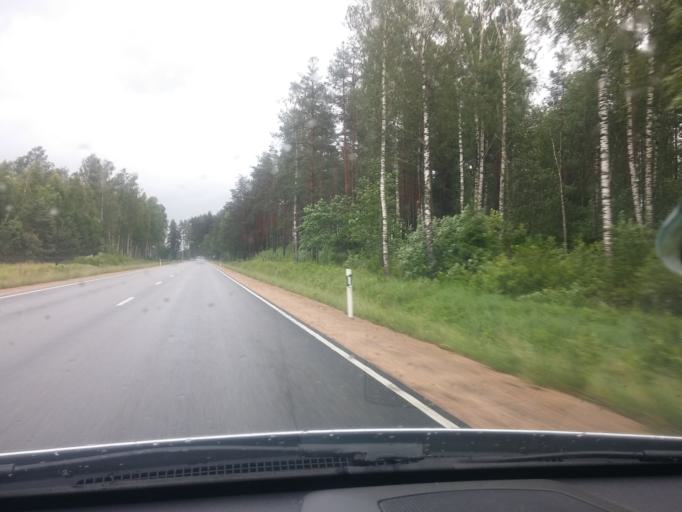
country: LV
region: Salaspils
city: Salaspils
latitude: 56.9034
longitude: 24.3950
